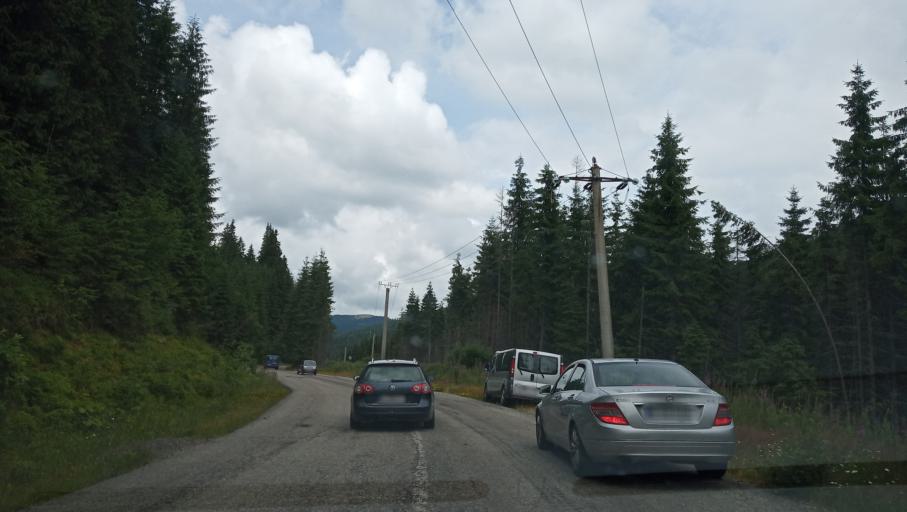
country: RO
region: Gorj
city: Novaci-Straini
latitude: 45.4303
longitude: 23.6772
